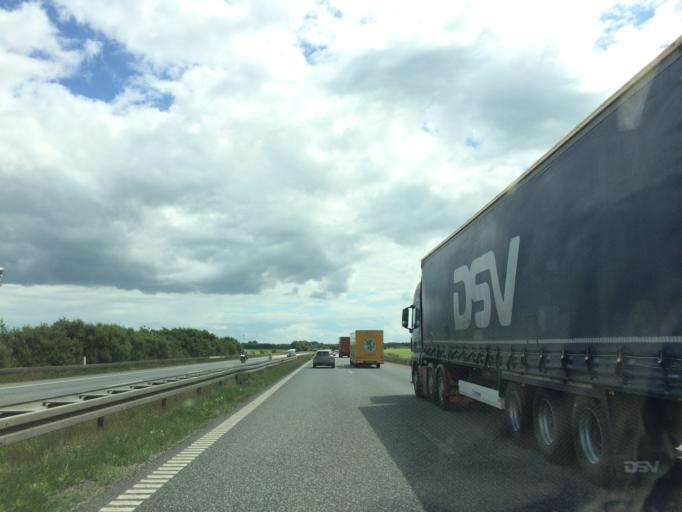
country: DK
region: North Denmark
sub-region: Mariagerfjord Kommune
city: Hobro
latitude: 56.7225
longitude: 9.7174
